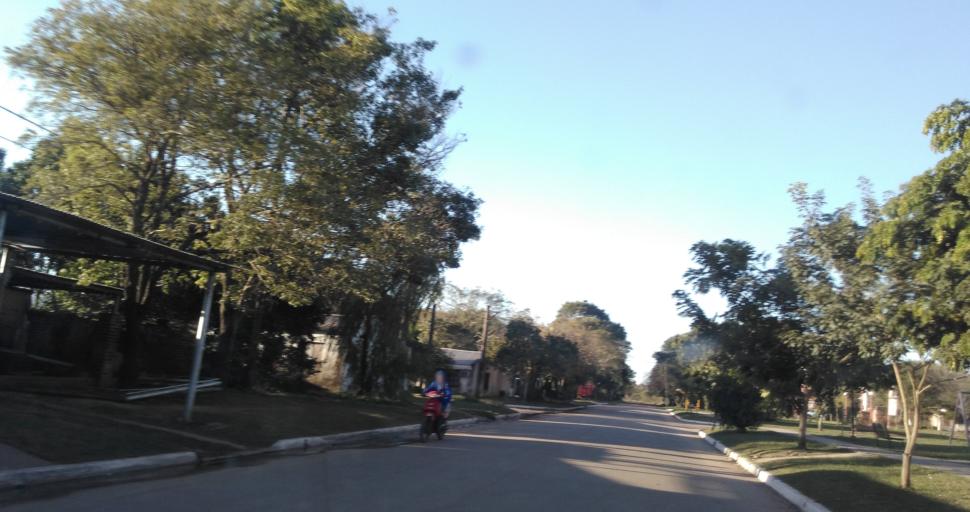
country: AR
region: Chaco
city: Colonia Benitez
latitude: -27.3318
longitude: -58.9457
